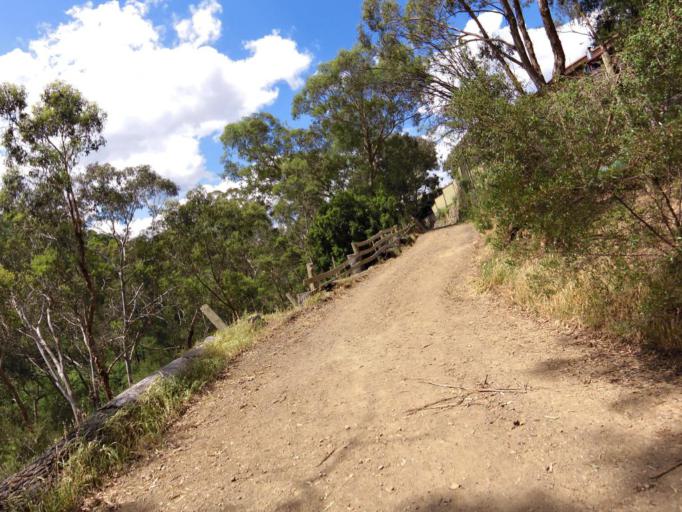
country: AU
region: Victoria
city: Plenty
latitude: -37.6830
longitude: 145.1041
